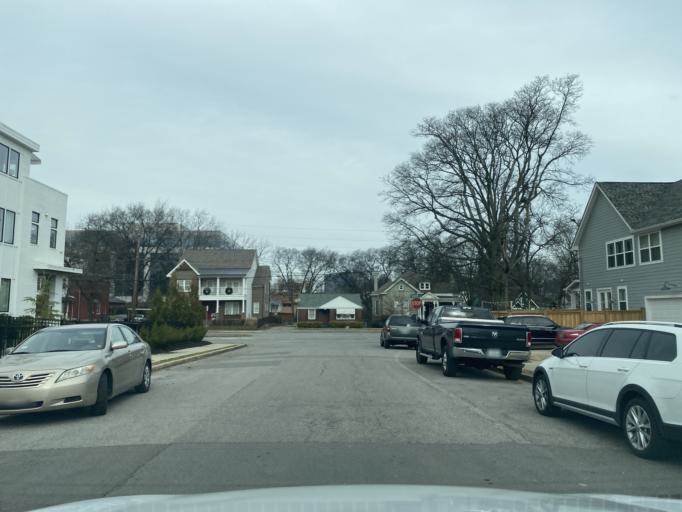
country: US
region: Tennessee
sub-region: Davidson County
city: Nashville
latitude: 36.1473
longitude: -86.7900
